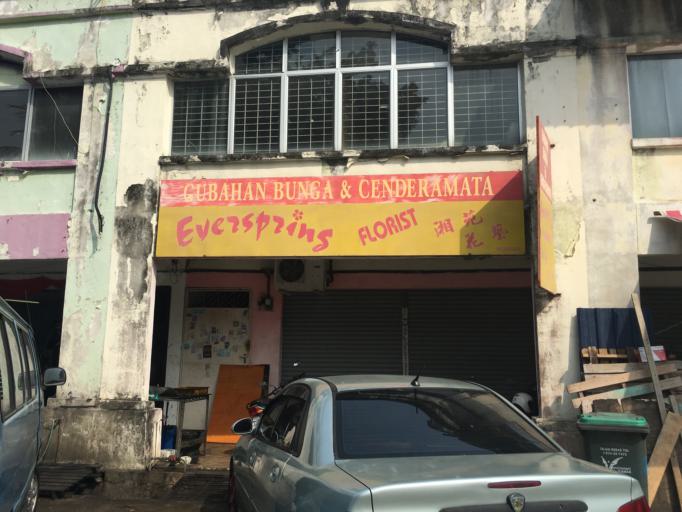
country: MY
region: Kedah
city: Kulim
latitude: 5.3880
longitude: 100.5637
